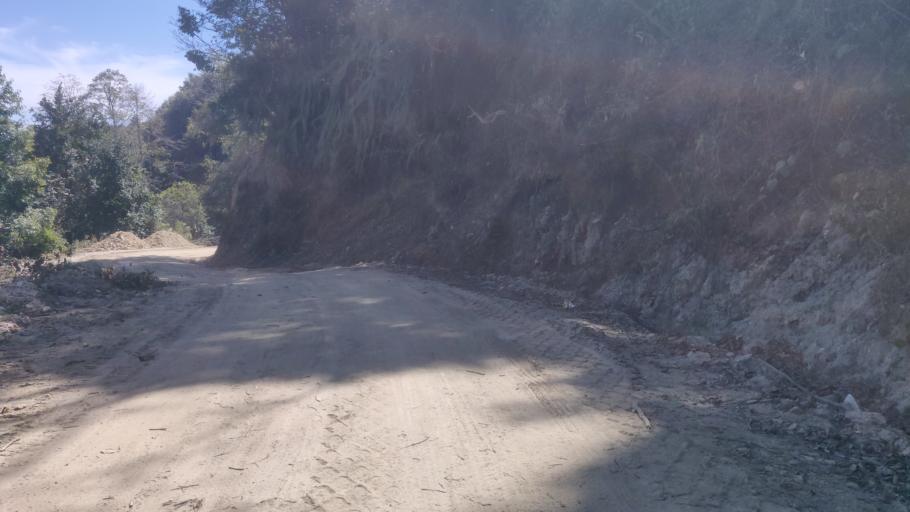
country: NP
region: Central Region
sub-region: Bagmati Zone
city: Nagarkot
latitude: 27.7846
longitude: 85.4816
